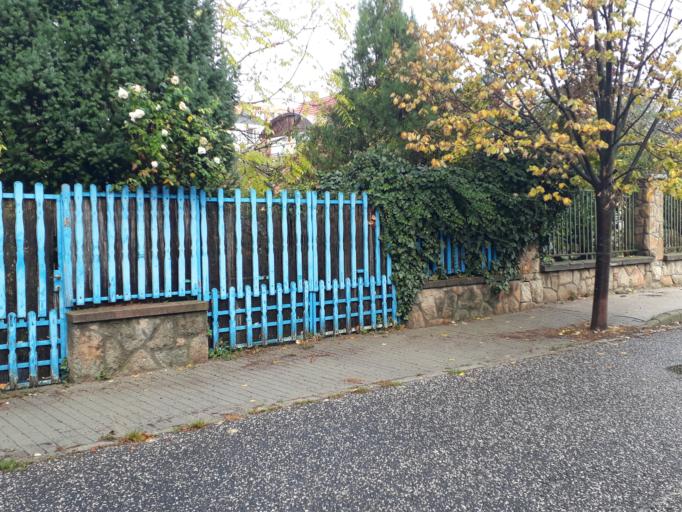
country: HU
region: Budapest
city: Budapest XII. keruelet
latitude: 47.4654
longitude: 19.0095
